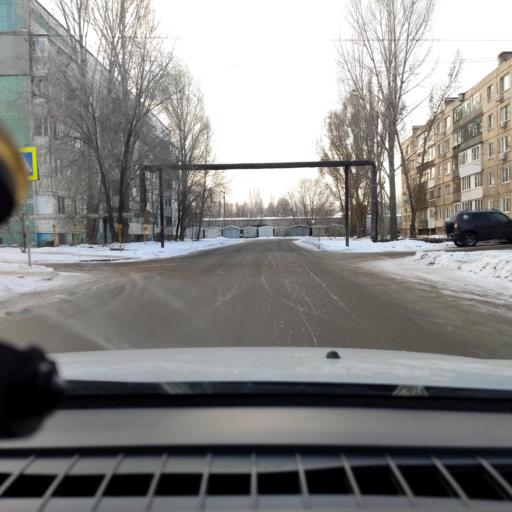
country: RU
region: Samara
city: Samara
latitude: 53.1209
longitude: 50.0946
